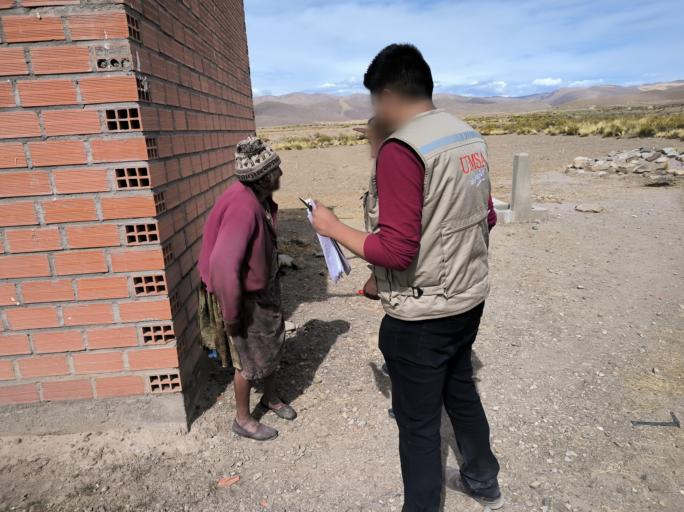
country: BO
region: Oruro
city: Challapata
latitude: -19.1203
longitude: -66.7683
